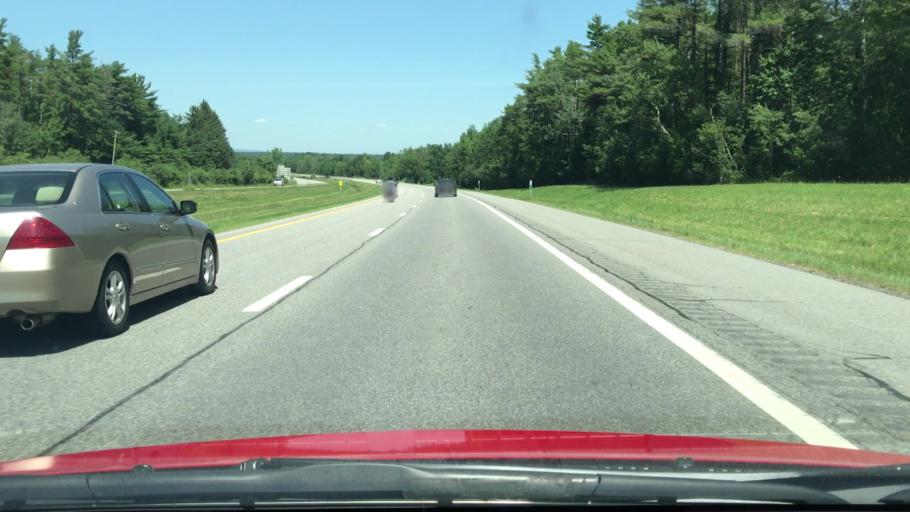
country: US
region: New York
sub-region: Essex County
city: Keeseville
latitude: 44.4618
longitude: -73.4849
